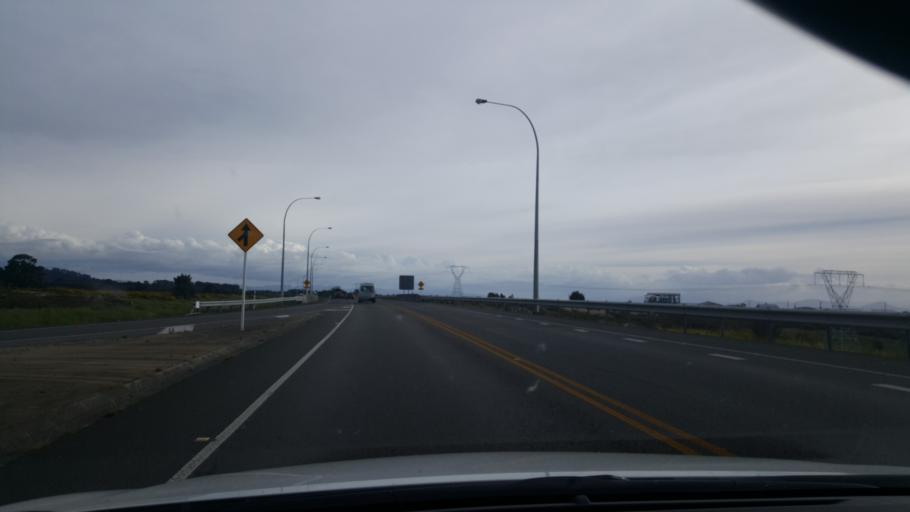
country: NZ
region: Waikato
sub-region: Taupo District
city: Taupo
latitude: -38.6832
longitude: 176.1147
